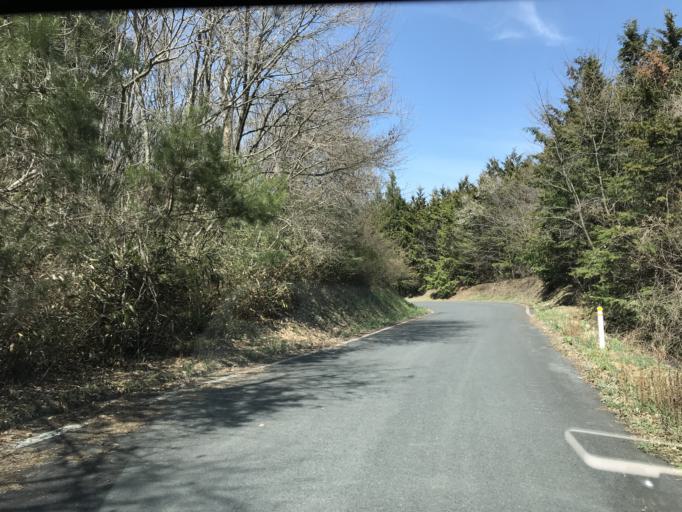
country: JP
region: Iwate
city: Ichinoseki
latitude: 38.8367
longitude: 141.2871
